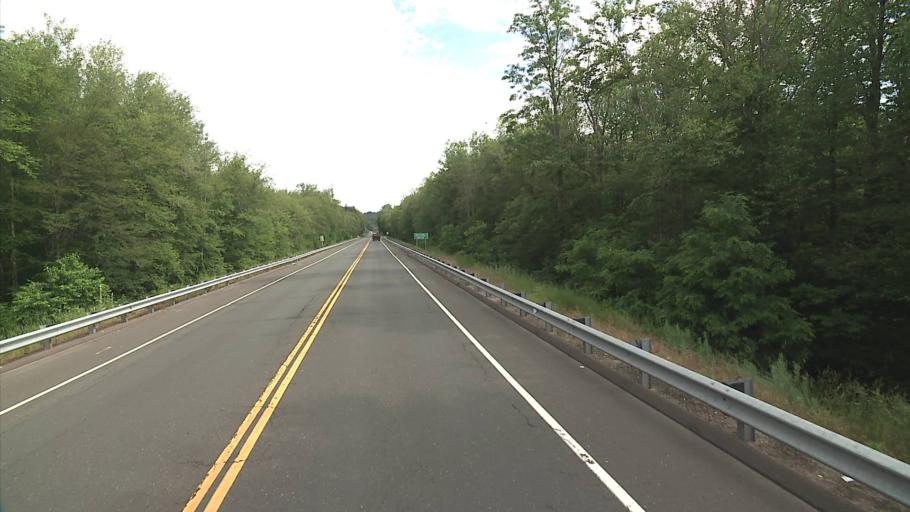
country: US
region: Connecticut
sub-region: New Haven County
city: Middlebury
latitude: 41.5240
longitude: -73.0825
